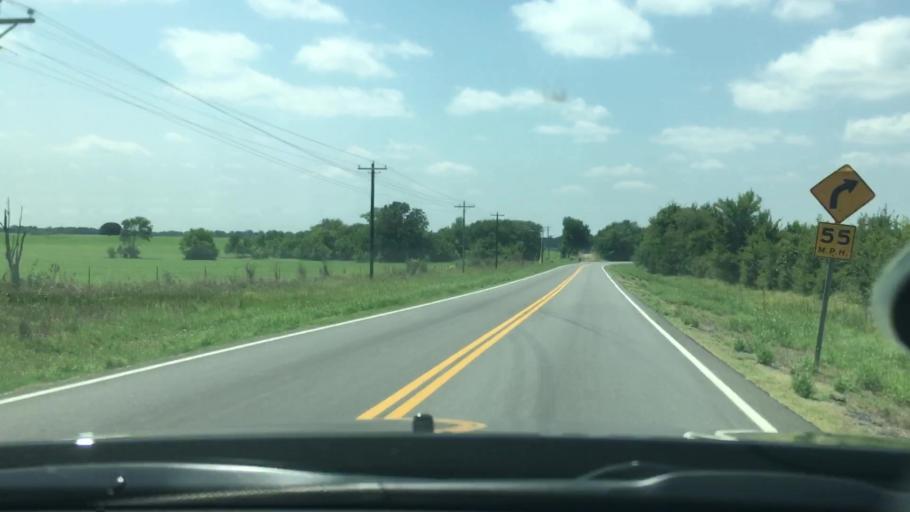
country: US
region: Oklahoma
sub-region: Atoka County
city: Atoka
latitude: 34.3749
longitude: -96.2554
